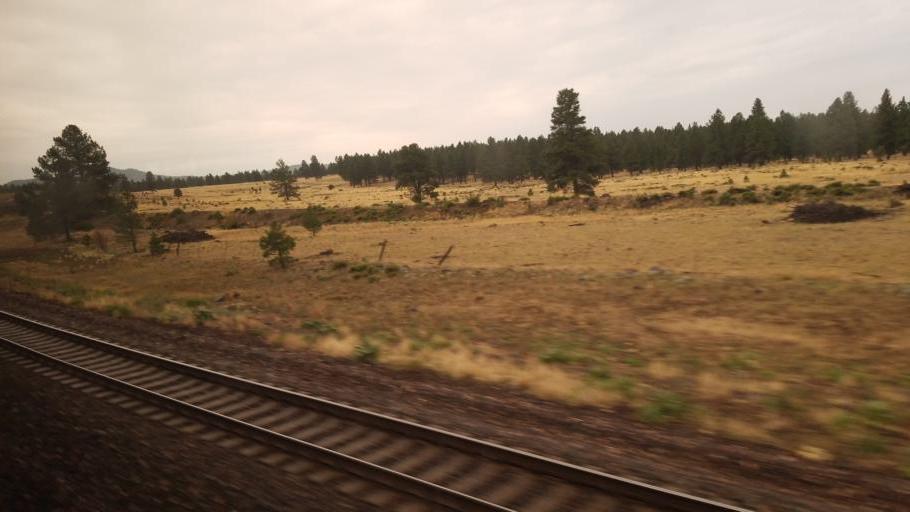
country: US
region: Arizona
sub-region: Coconino County
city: Parks
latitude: 35.2417
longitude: -111.9899
